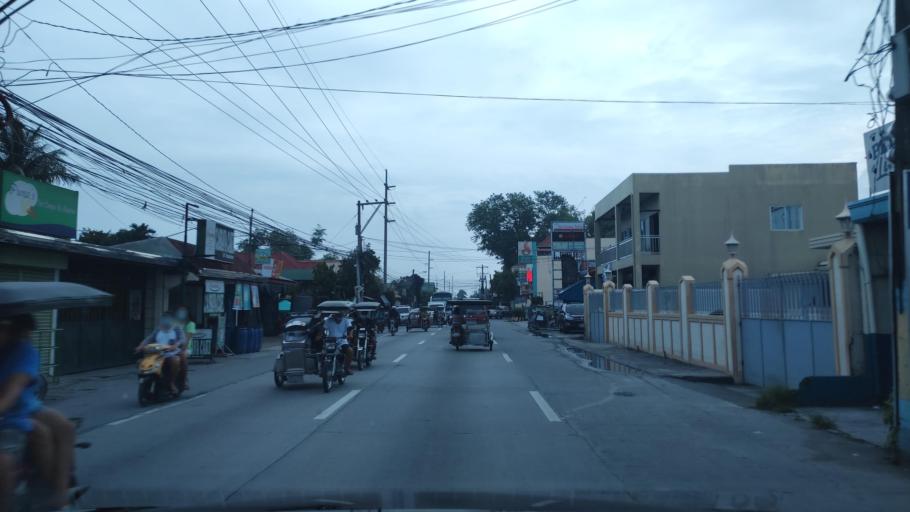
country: PH
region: Central Luzon
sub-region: Province of Pampanga
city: Santa Ana
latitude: 15.0971
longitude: 120.7677
